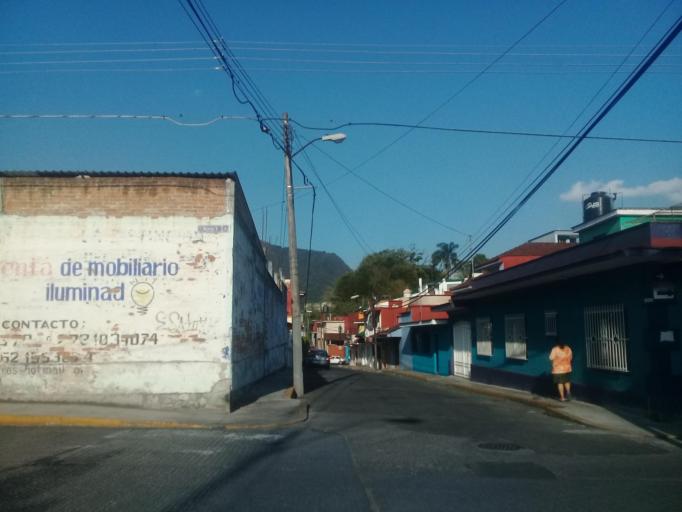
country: MX
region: Veracruz
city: Orizaba
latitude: 18.8551
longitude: -97.1088
